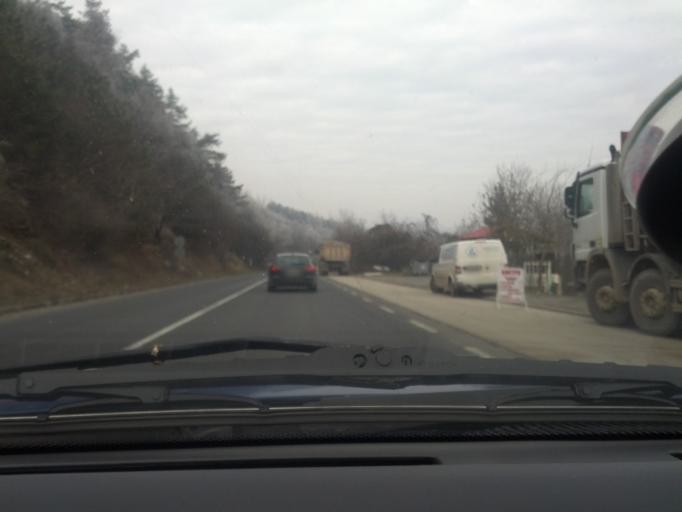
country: BG
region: Sofiya
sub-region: Obshtina Botevgrad
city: Botevgrad
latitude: 42.9540
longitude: 23.7638
